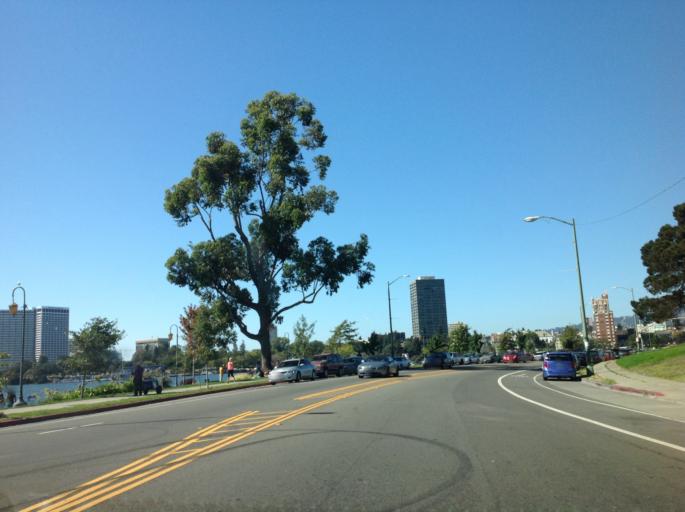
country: US
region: California
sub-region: Alameda County
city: Oakland
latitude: 37.8013
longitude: -122.2542
